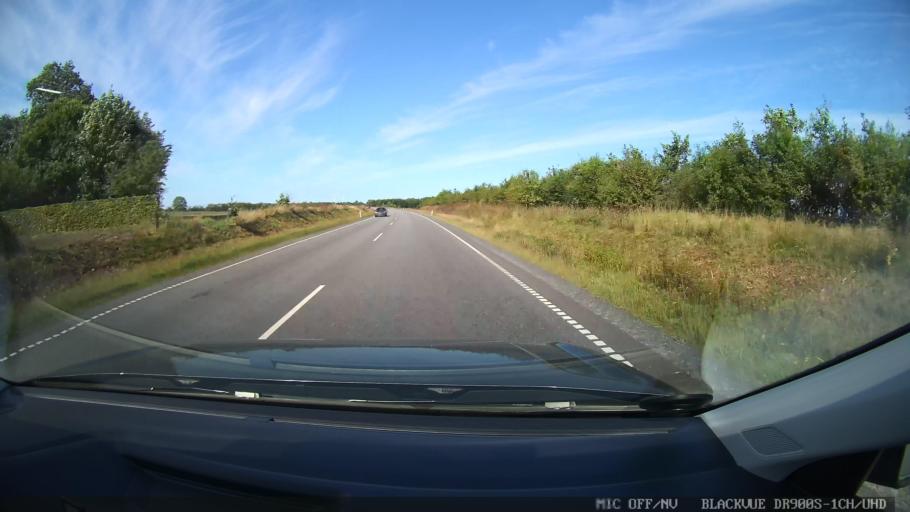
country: DK
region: North Denmark
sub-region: Mariagerfjord Kommune
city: Hobro
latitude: 56.6650
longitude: 9.7725
